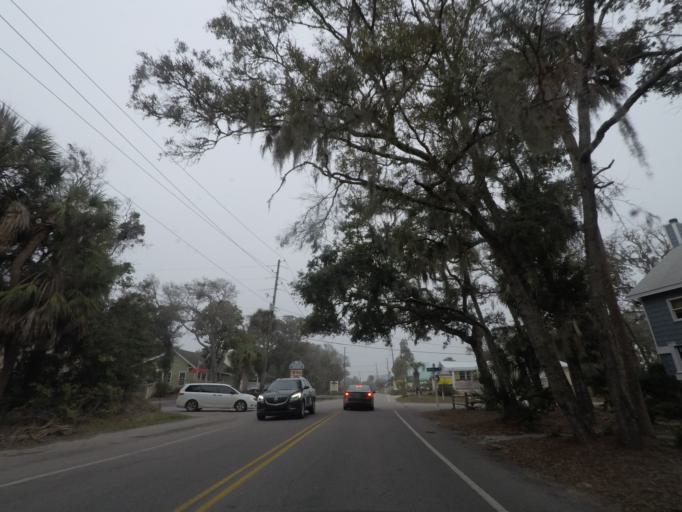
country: US
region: South Carolina
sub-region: Charleston County
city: Seabrook Island
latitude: 32.5011
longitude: -80.3030
